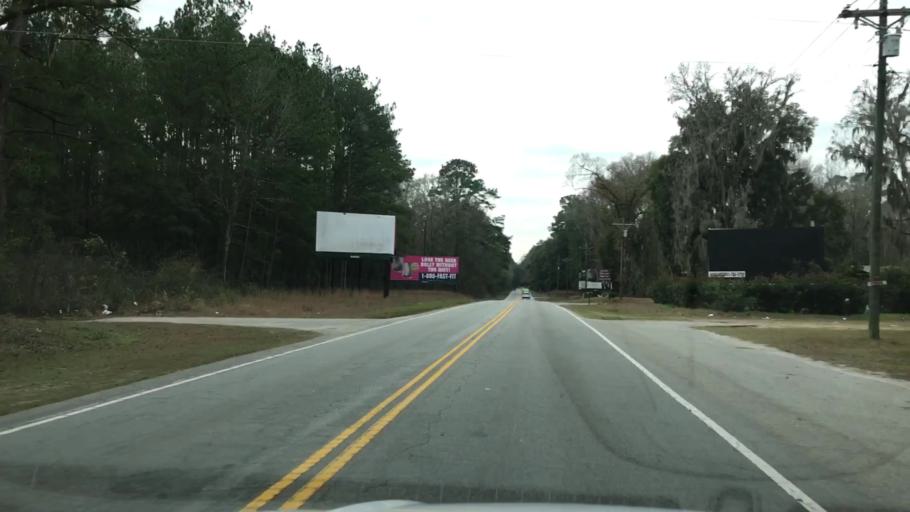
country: US
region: South Carolina
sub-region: Jasper County
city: Ridgeland
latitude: 32.3950
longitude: -80.9072
